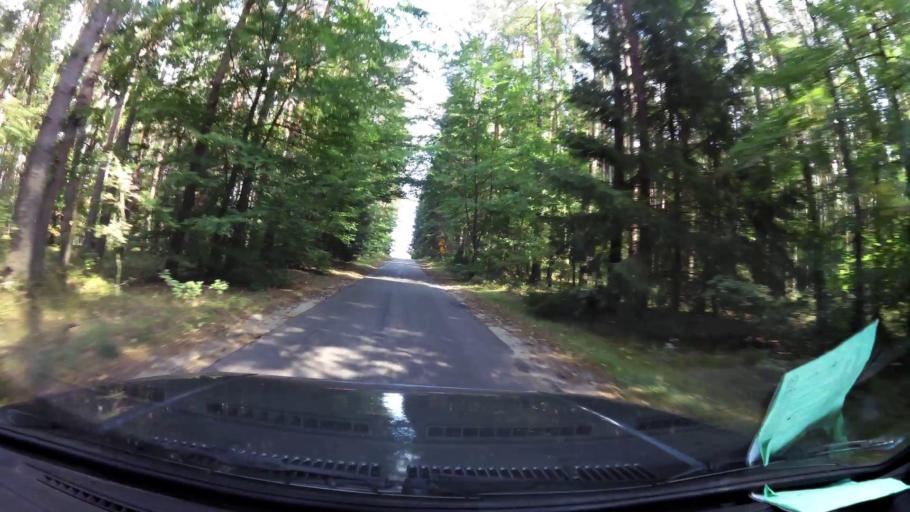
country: PL
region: West Pomeranian Voivodeship
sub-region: Powiat koszalinski
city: Bobolice
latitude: 54.0829
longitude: 16.4748
